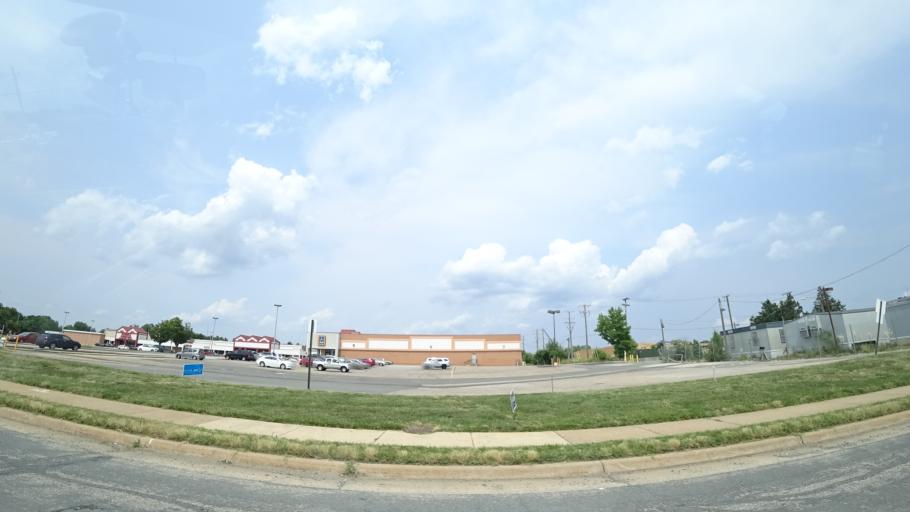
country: US
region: Virginia
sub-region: Prince William County
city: Woodbridge
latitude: 38.6632
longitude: -77.2488
